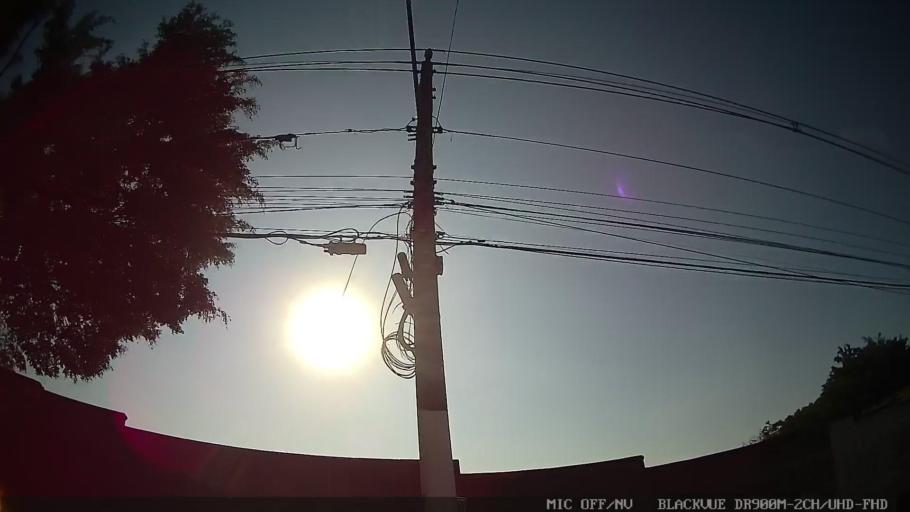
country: BR
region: Sao Paulo
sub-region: Ferraz De Vasconcelos
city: Ferraz de Vasconcelos
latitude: -23.5529
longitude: -46.4368
